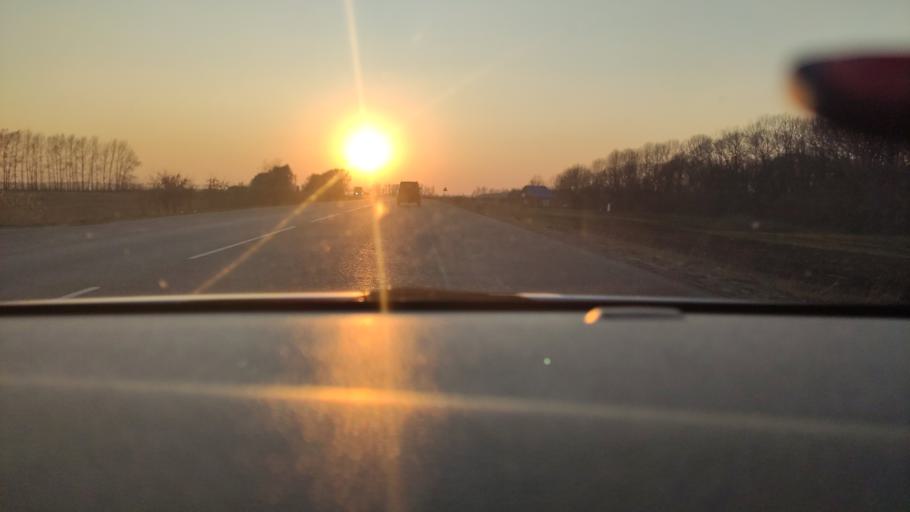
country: RU
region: Voronezj
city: Kolodeznyy
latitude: 51.3404
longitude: 39.0388
